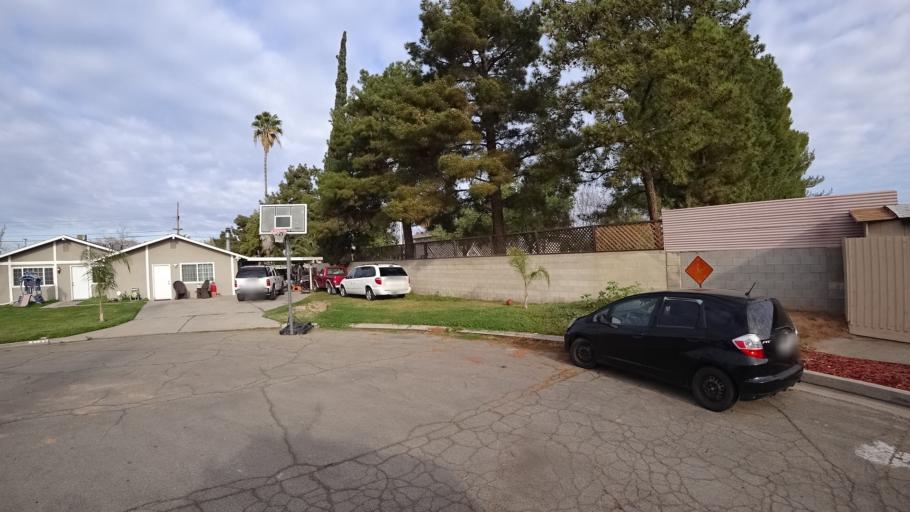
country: US
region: California
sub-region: Fresno County
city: Fresno
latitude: 36.8337
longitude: -119.7970
